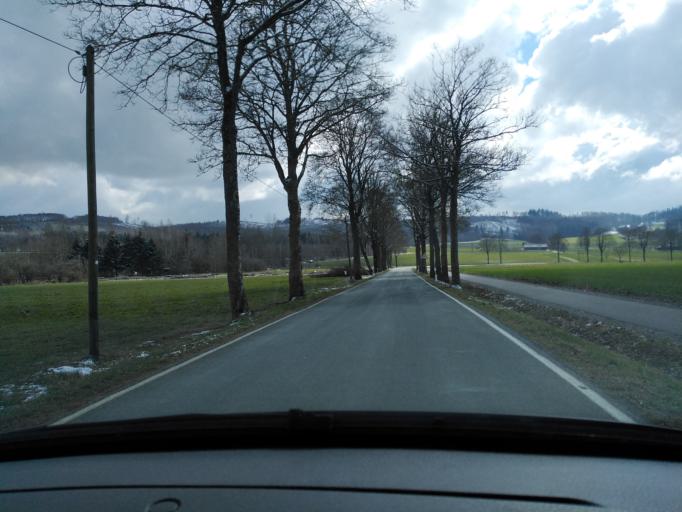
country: DE
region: North Rhine-Westphalia
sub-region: Regierungsbezirk Arnsberg
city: Brilon
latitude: 51.4009
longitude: 8.6332
